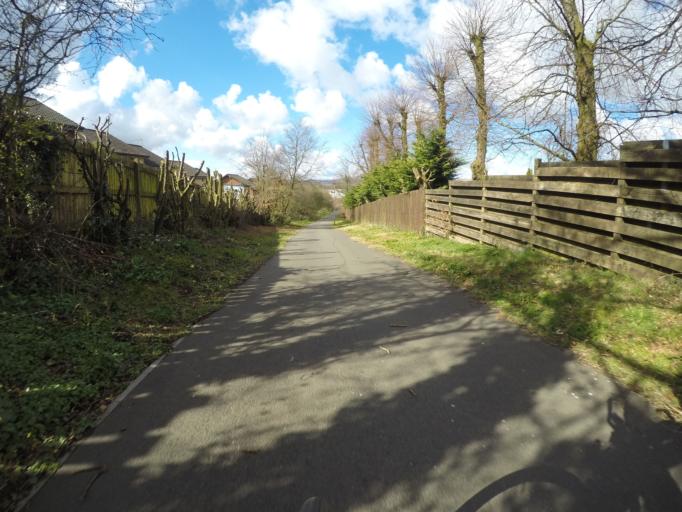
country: GB
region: Scotland
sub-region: North Ayrshire
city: Beith
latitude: 55.7446
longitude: -4.6434
